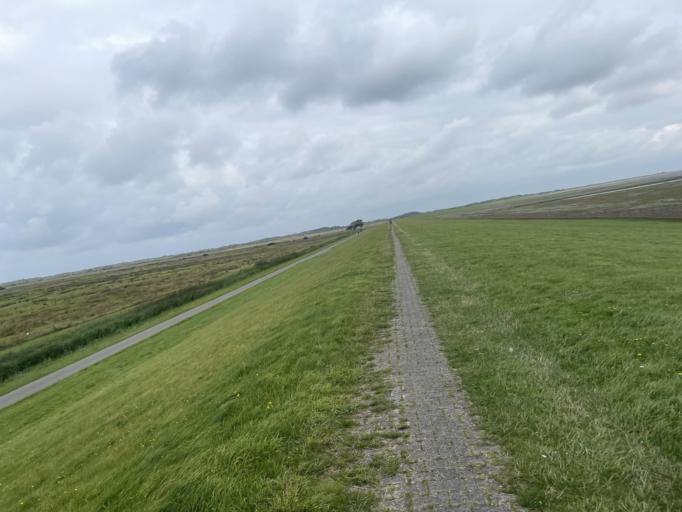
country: DE
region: Lower Saxony
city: Borkum
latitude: 53.5899
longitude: 6.7366
